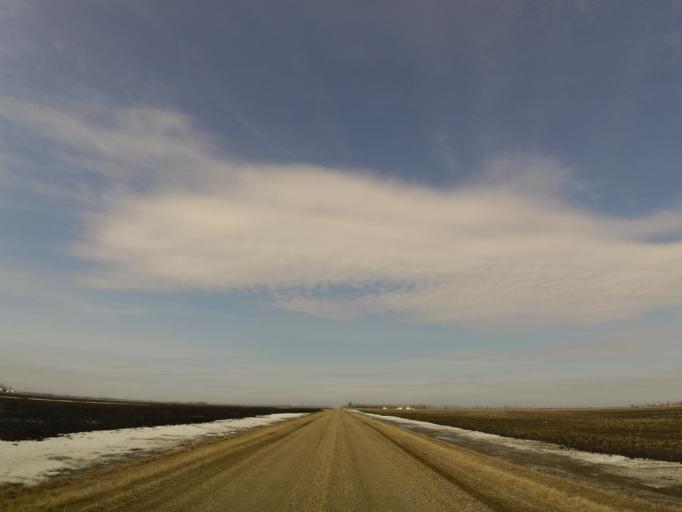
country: US
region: North Dakota
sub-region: Walsh County
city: Grafton
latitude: 48.4143
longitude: -97.2553
